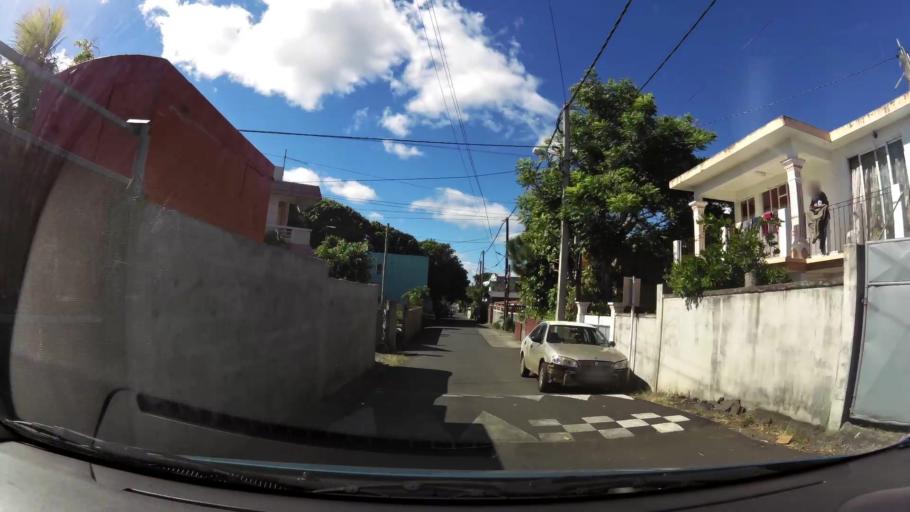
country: MU
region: Plaines Wilhems
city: Vacoas
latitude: -20.3087
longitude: 57.4802
